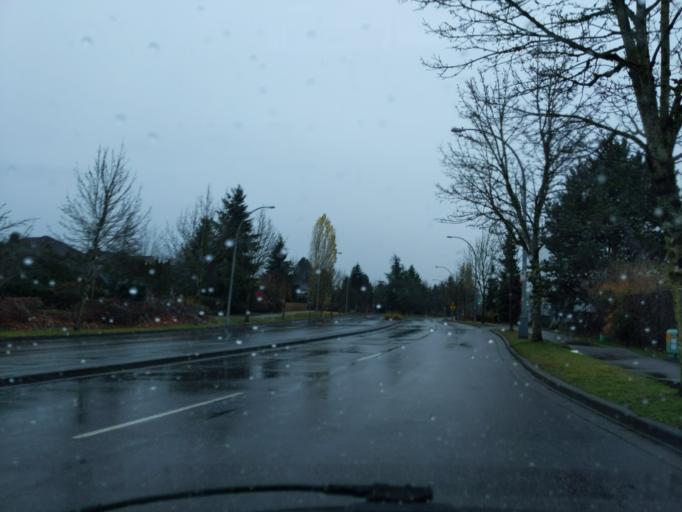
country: CA
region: British Columbia
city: Walnut Grove
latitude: 49.1706
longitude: -122.6633
